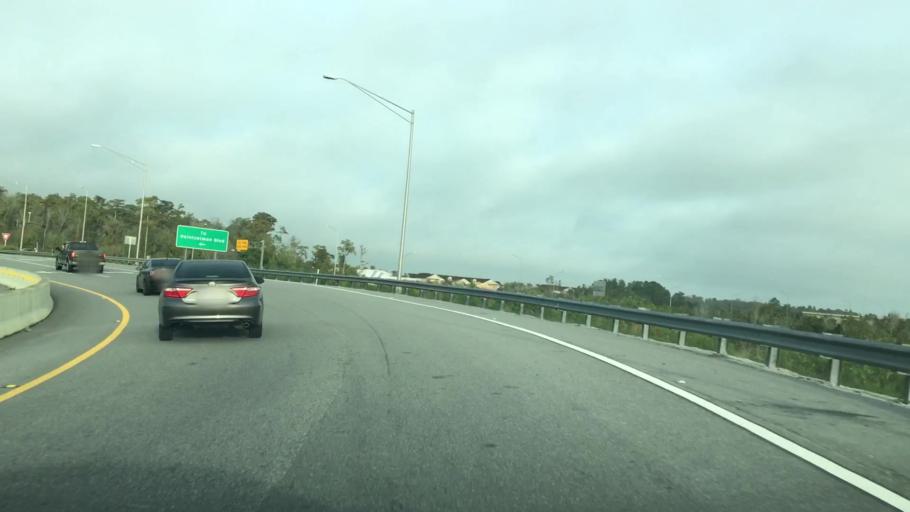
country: US
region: Florida
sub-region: Orange County
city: Conway
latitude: 28.4508
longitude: -81.2846
